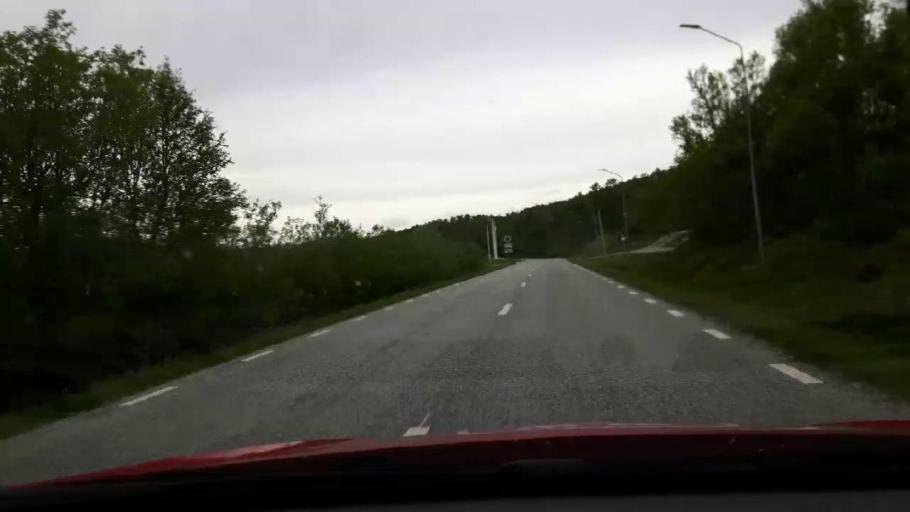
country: NO
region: Sor-Trondelag
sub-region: Tydal
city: Aas
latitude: 62.5977
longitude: 12.1811
